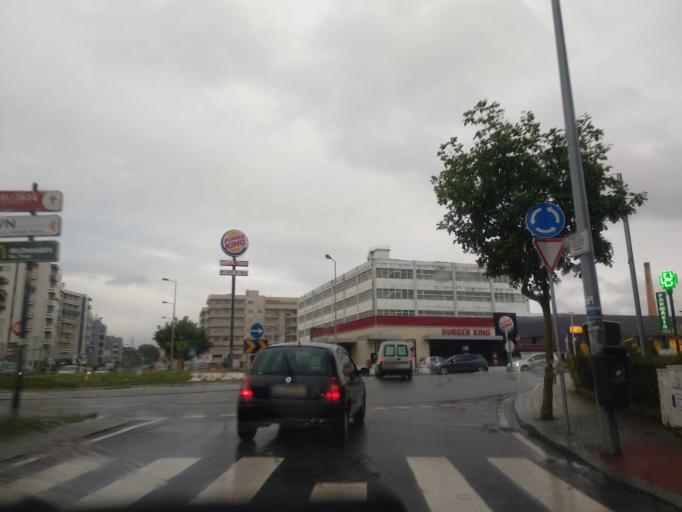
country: PT
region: Porto
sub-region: Gondomar
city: Rio Tinto
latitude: 41.1737
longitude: -8.5556
